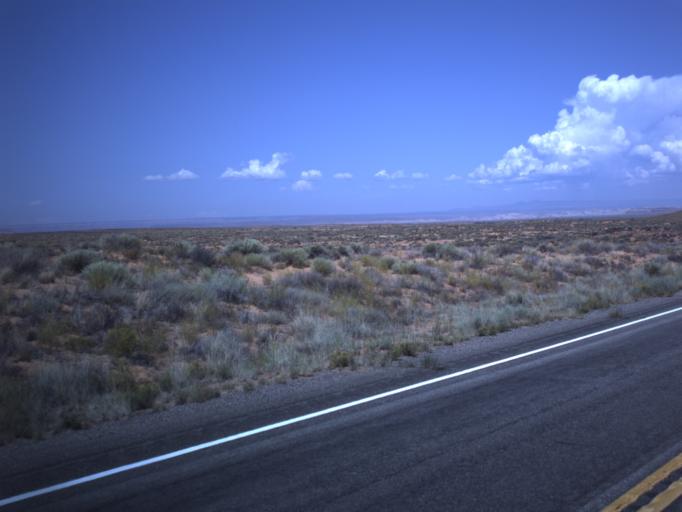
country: US
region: Utah
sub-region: San Juan County
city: Blanding
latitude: 37.0884
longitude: -109.5479
